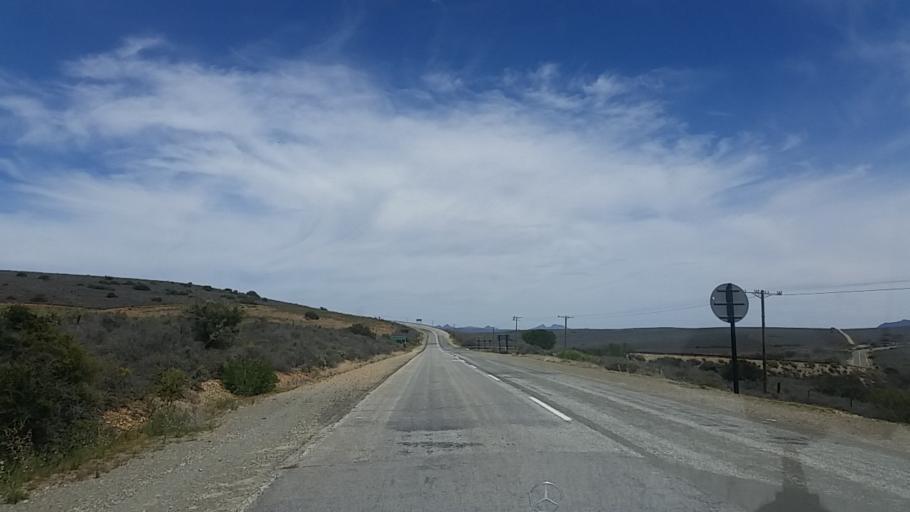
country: ZA
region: Western Cape
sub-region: Eden District Municipality
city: Knysna
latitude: -33.6265
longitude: 23.1319
